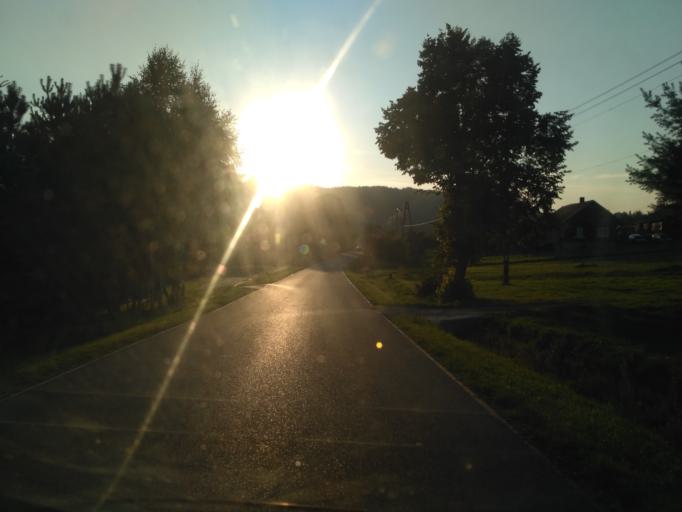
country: PL
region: Subcarpathian Voivodeship
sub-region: Powiat krosnienski
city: Odrzykon
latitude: 49.7778
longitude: 21.7712
